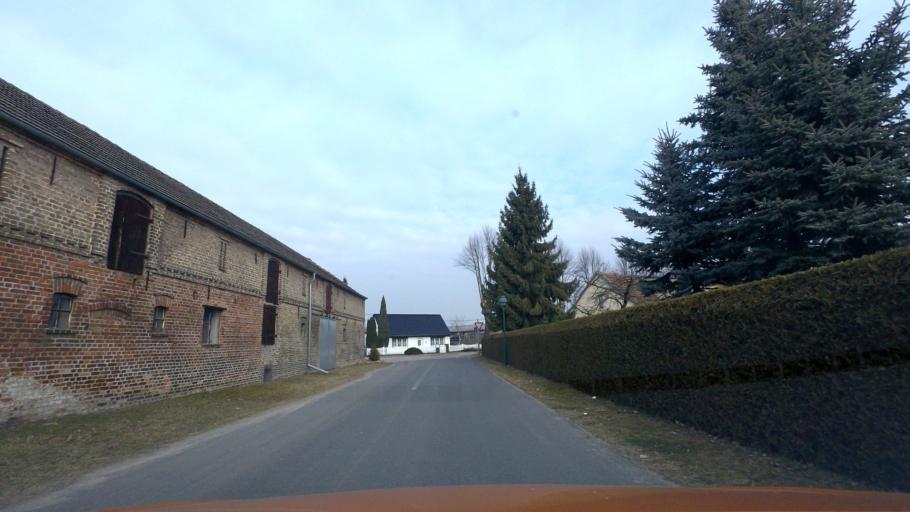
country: DE
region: Brandenburg
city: Trebbin
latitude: 52.2201
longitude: 13.2011
